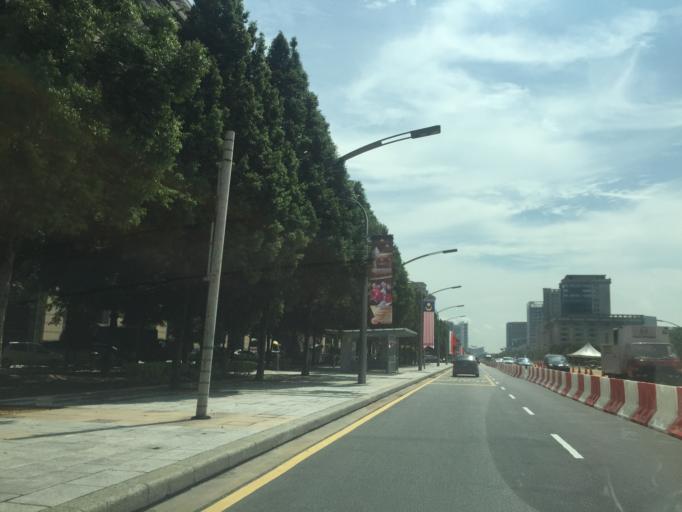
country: MY
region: Putrajaya
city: Putrajaya
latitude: 2.9257
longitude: 101.6880
